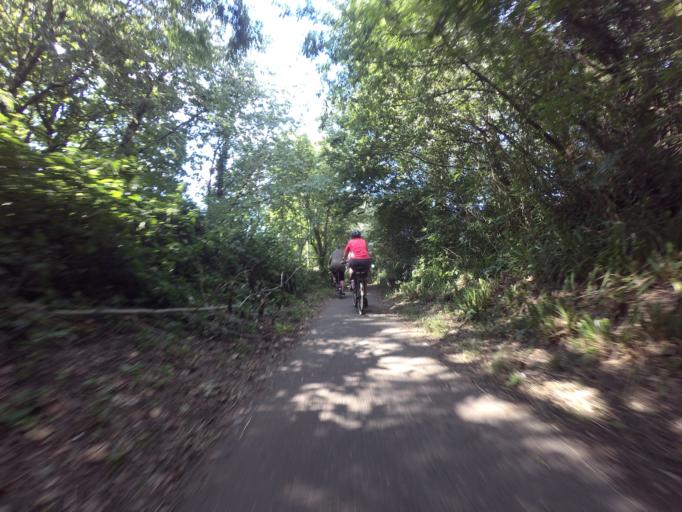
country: GB
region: England
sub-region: East Sussex
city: Hailsham
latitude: 50.8670
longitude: 0.2543
